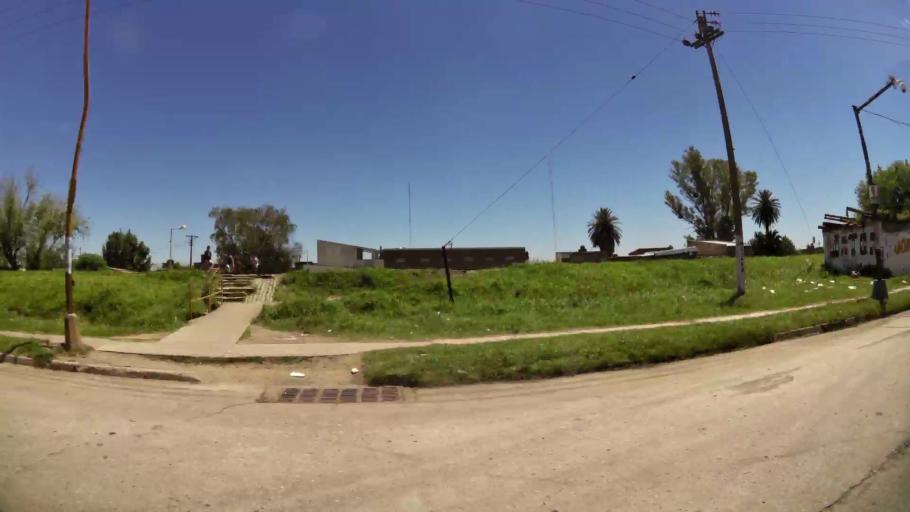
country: AR
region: Santa Fe
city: Santa Fe de la Vera Cruz
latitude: -31.6320
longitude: -60.7203
